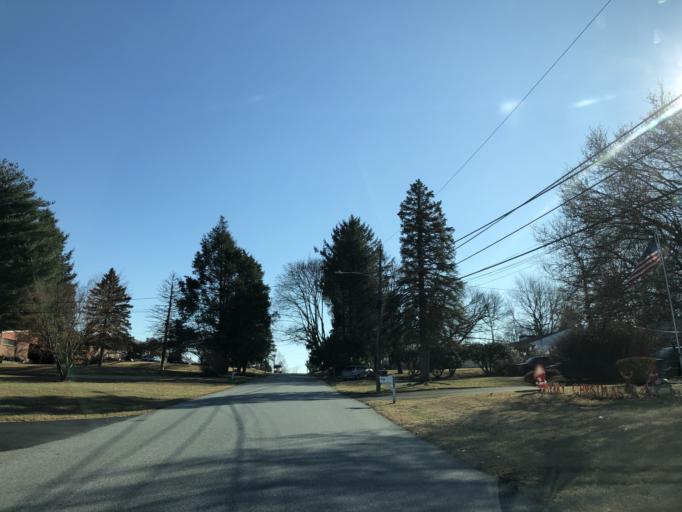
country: US
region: Pennsylvania
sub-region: Delaware County
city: Boothwyn
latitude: 39.8481
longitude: -75.4441
